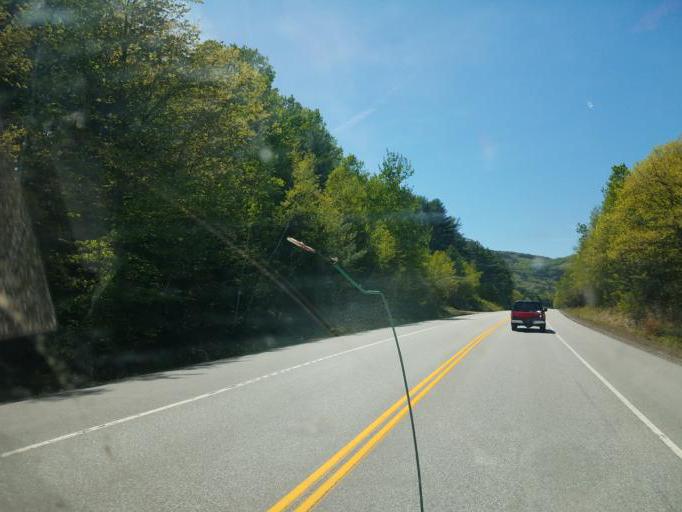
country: US
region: New Hampshire
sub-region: Grafton County
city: Rumney
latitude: 43.7948
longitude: -71.8321
